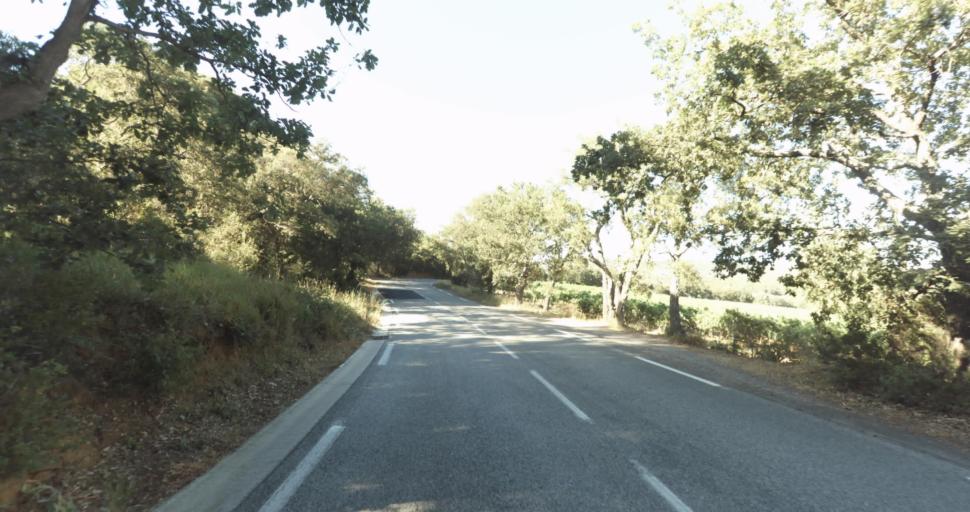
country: FR
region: Provence-Alpes-Cote d'Azur
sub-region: Departement du Var
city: Gassin
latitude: 43.2420
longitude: 6.5880
